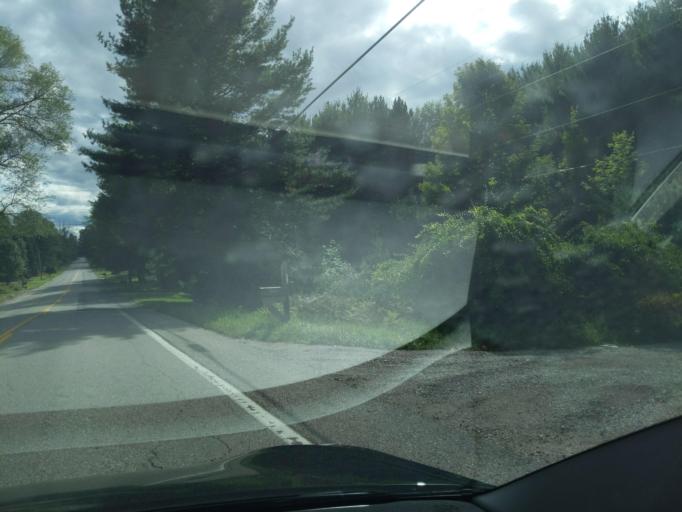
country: US
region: Michigan
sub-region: Antrim County
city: Bellaire
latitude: 44.9267
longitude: -85.2857
